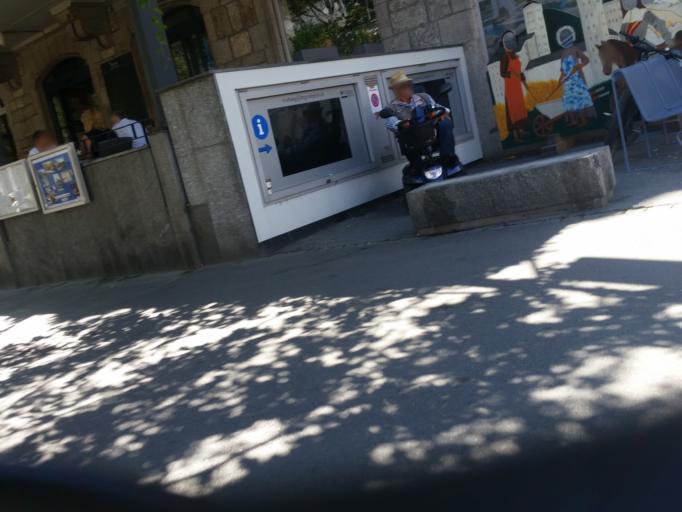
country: CH
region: Valais
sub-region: Brig District
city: Brig
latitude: 46.3188
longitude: 7.9882
